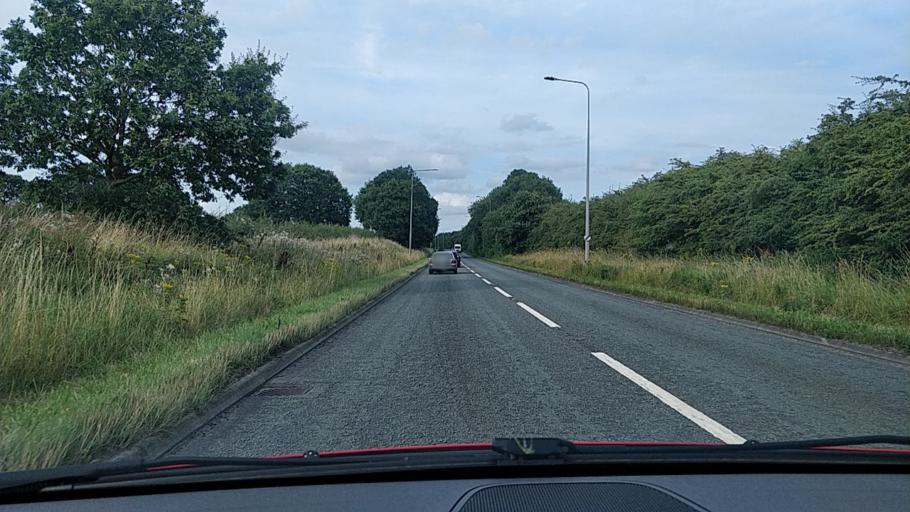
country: GB
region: Wales
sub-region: County of Flintshire
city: Penyffordd
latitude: 53.1503
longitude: -3.0483
